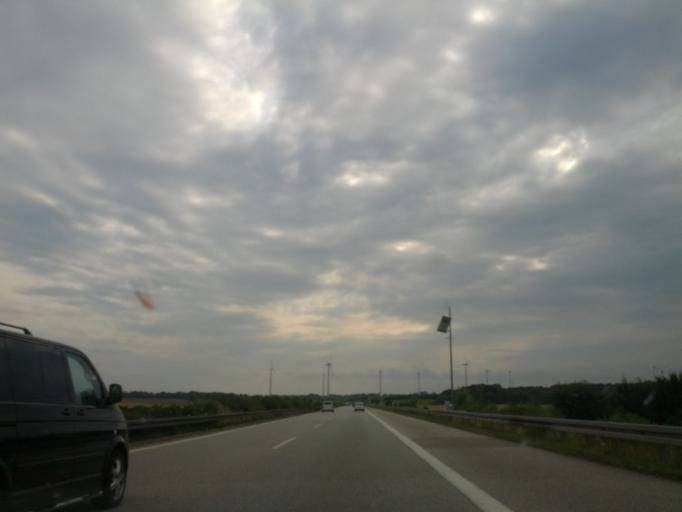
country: DE
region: Mecklenburg-Vorpommern
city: Jurgenshagen
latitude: 53.9805
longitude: 11.9190
